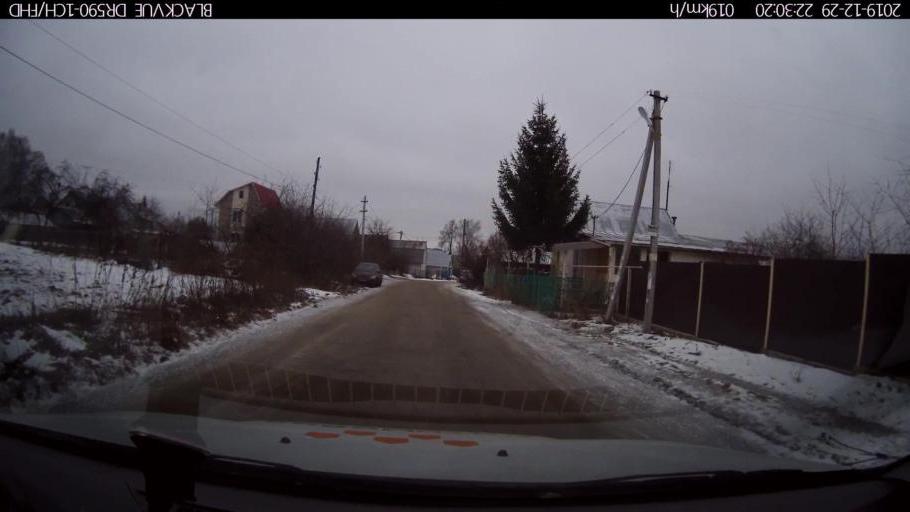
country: RU
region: Nizjnij Novgorod
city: Afonino
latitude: 56.2061
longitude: 43.9861
